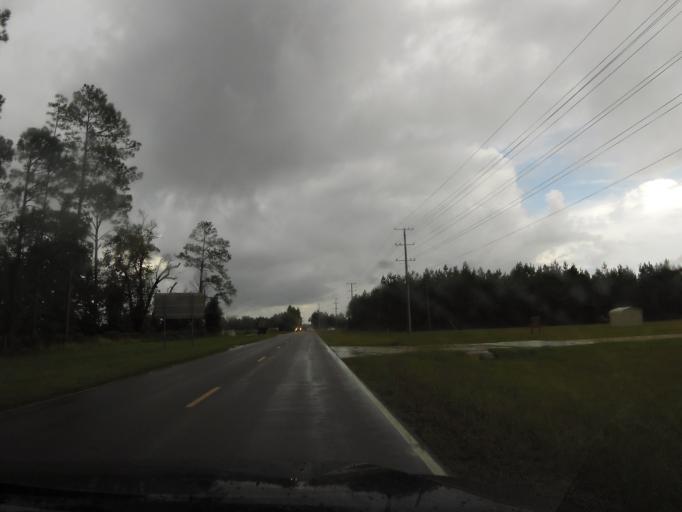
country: US
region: Florida
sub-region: Nassau County
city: Callahan
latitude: 30.5244
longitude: -81.9961
